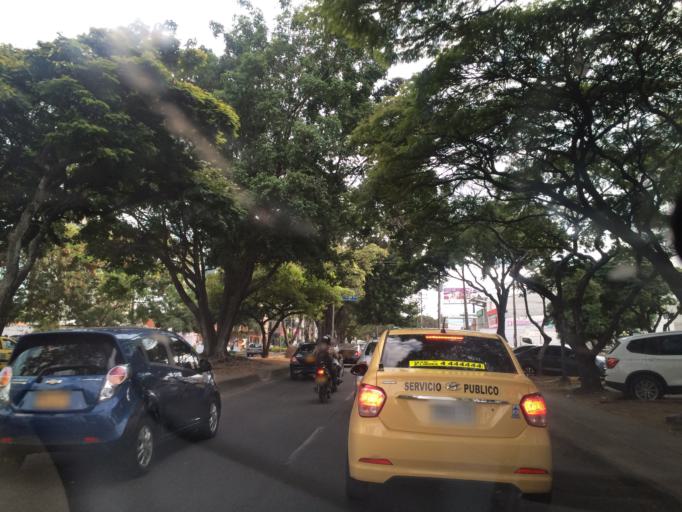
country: CO
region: Valle del Cauca
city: Cali
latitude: 3.4234
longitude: -76.5413
